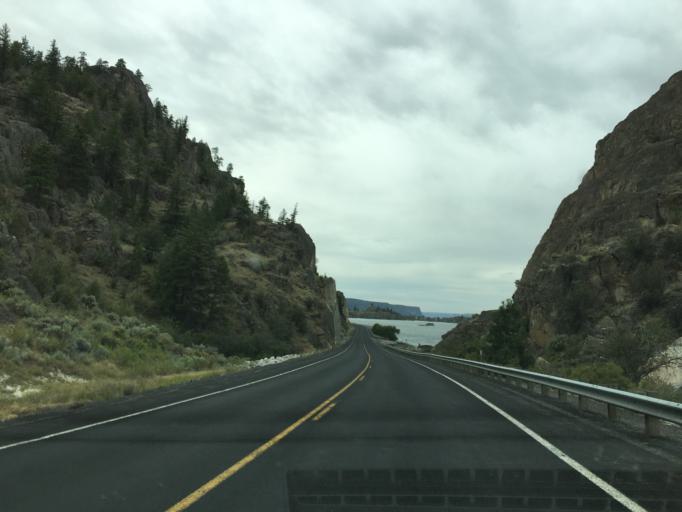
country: US
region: Washington
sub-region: Okanogan County
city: Coulee Dam
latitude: 47.8841
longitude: -119.0895
